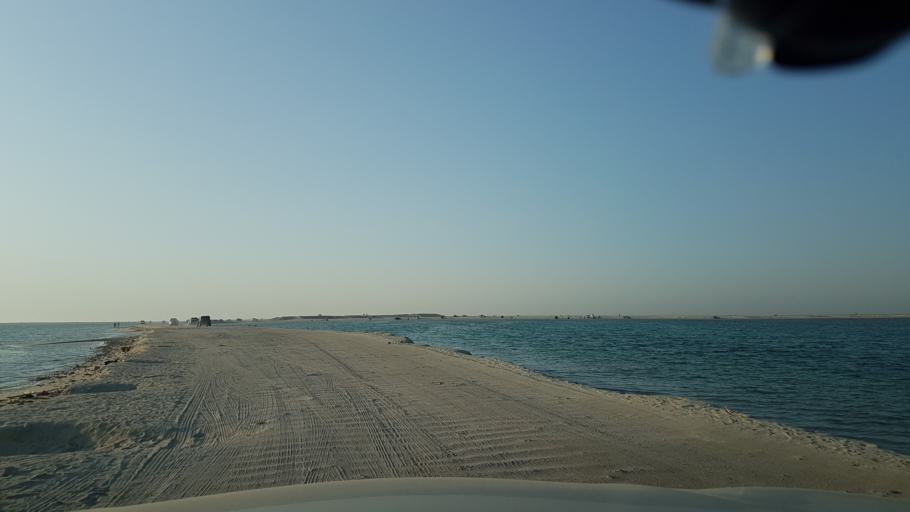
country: BH
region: Manama
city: Jidd Hafs
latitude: 26.2368
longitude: 50.5053
